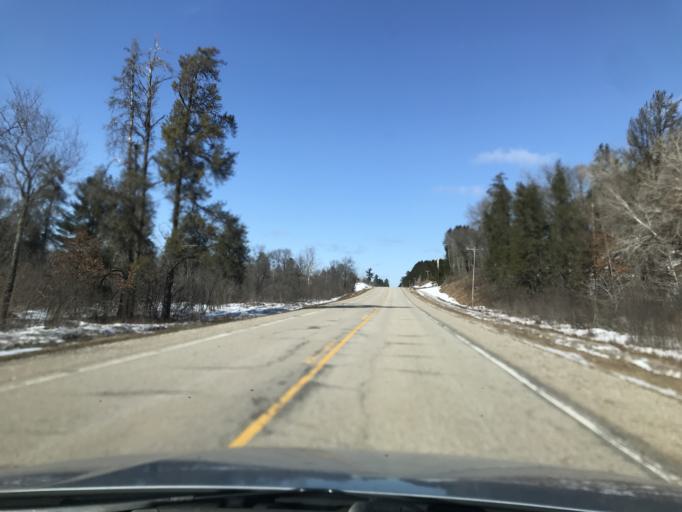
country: US
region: Wisconsin
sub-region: Marinette County
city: Niagara
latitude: 45.3749
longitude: -88.1000
